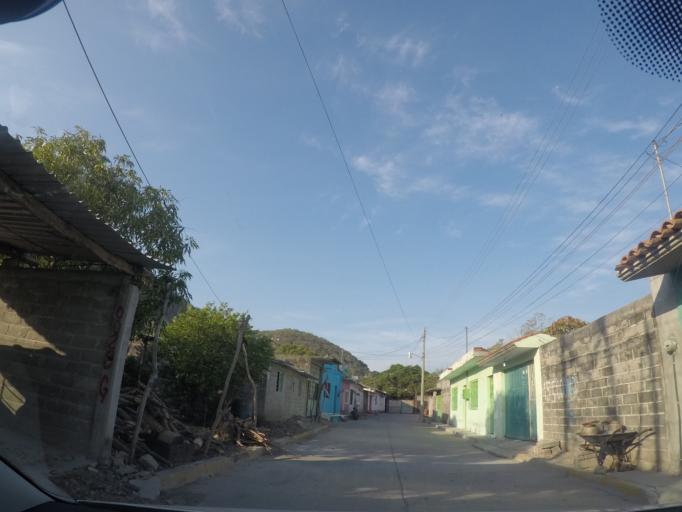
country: MX
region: Oaxaca
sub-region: Santo Domingo Tehuantepec
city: La Noria
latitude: 16.2457
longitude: -95.1512
